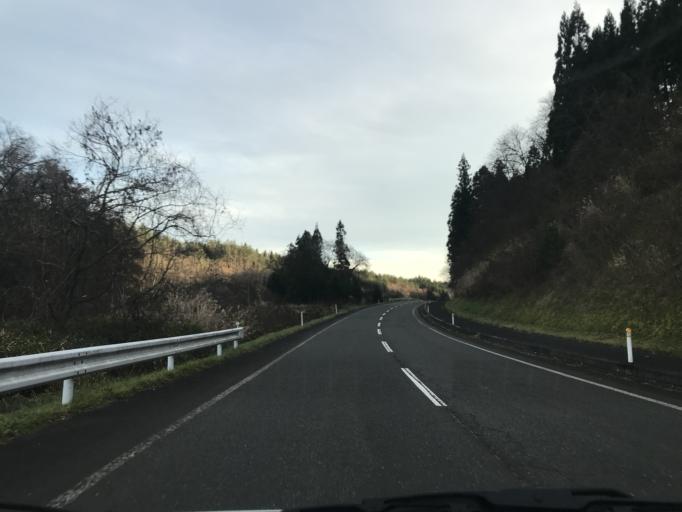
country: JP
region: Iwate
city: Ichinoseki
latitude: 38.9939
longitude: 141.0654
